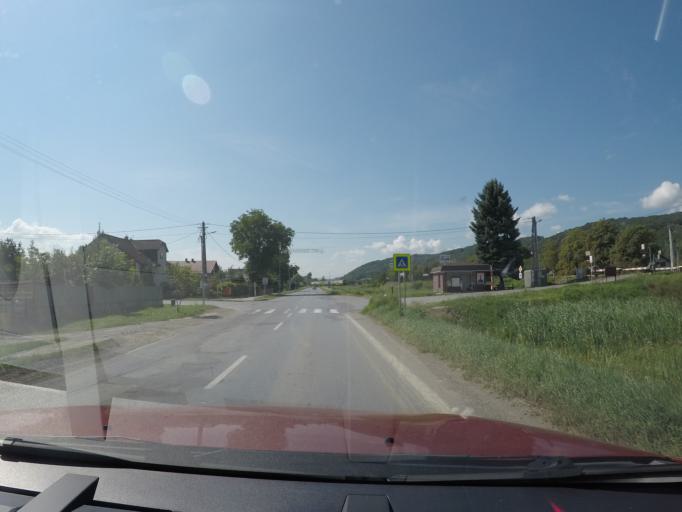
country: SK
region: Presovsky
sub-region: Okres Presov
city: Presov
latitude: 48.9578
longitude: 21.2414
